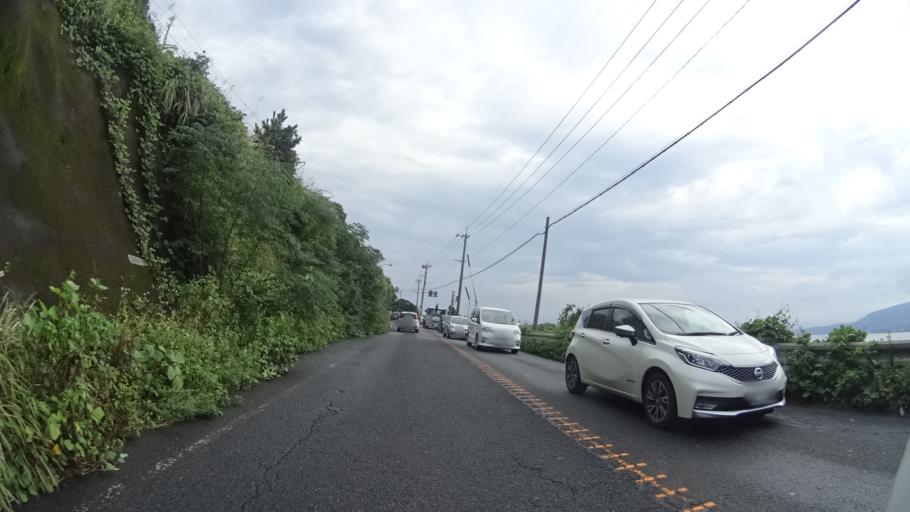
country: JP
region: Kagoshima
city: Kagoshima-shi
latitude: 31.6297
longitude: 130.5999
